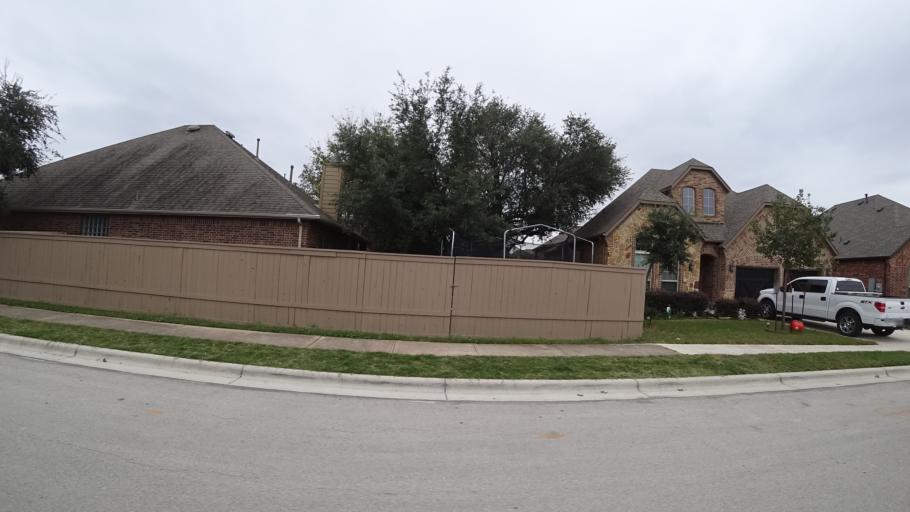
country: US
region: Texas
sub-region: Travis County
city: Manchaca
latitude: 30.1457
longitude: -97.8515
